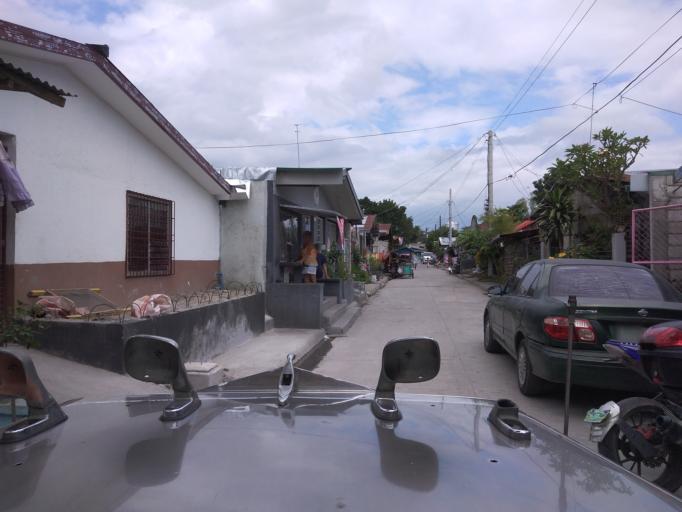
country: PH
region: Central Luzon
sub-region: Province of Pampanga
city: Pandacaqui
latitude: 15.1767
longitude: 120.6529
